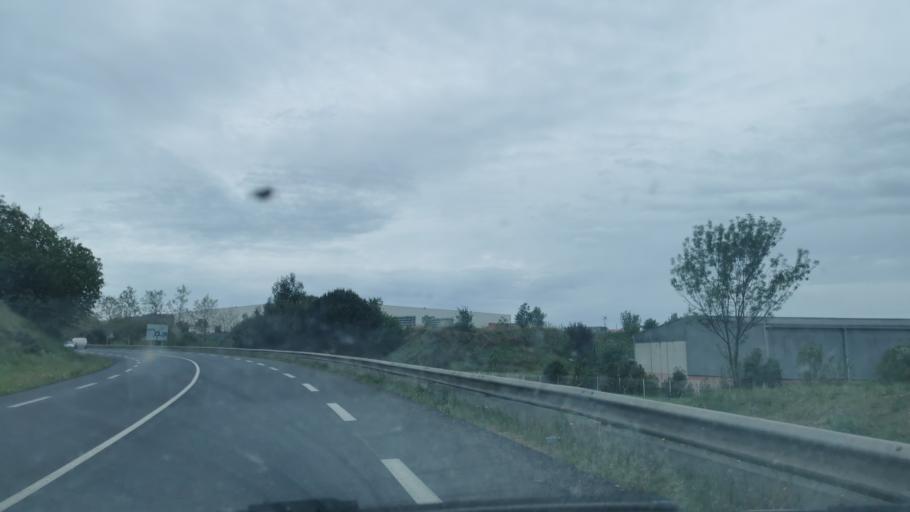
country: FR
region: Languedoc-Roussillon
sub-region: Departement de l'Herault
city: Gigean
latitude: 43.4911
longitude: 3.7015
